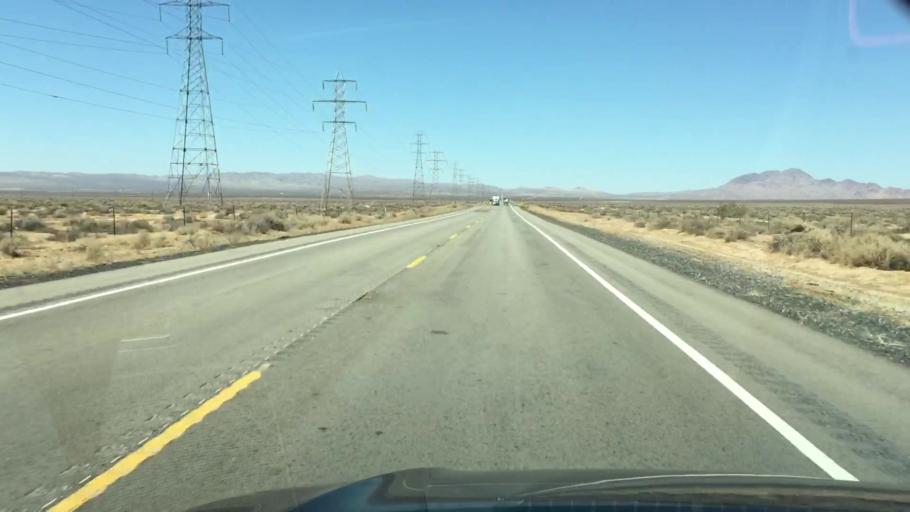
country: US
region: California
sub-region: Kern County
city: Boron
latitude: 35.1897
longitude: -117.5973
